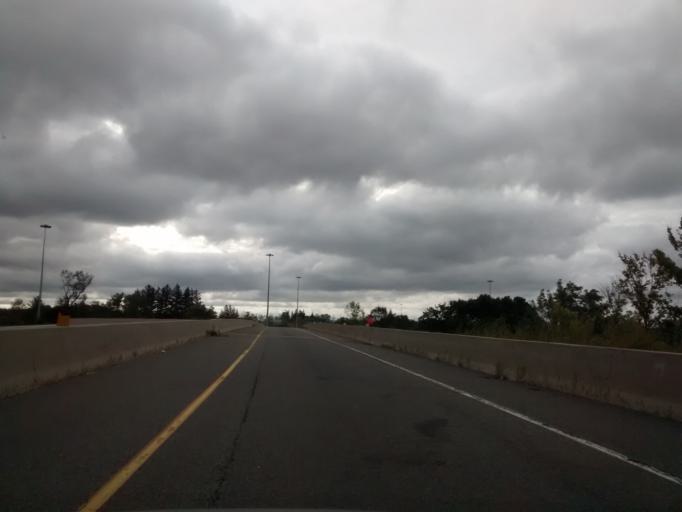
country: CA
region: Ontario
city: Ancaster
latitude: 43.2104
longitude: -79.9715
